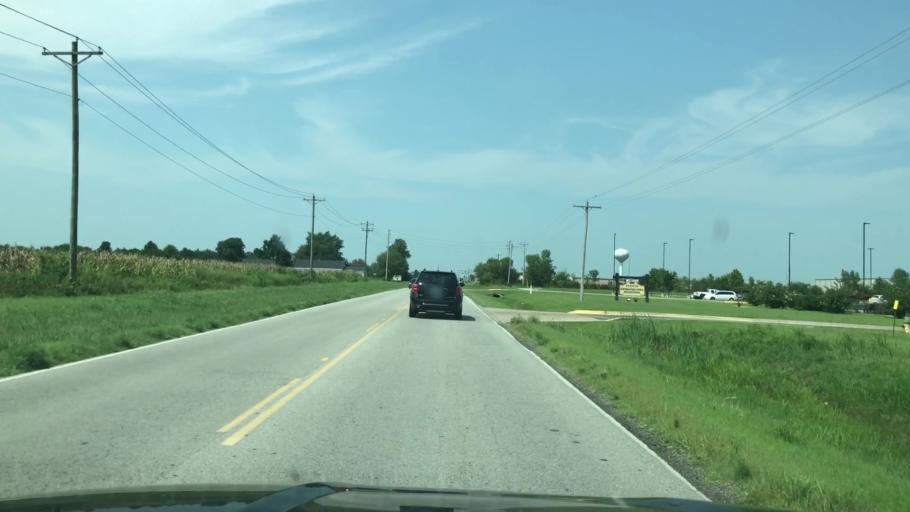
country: US
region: Oklahoma
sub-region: Ottawa County
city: Commerce
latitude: 36.9054
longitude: -94.8419
